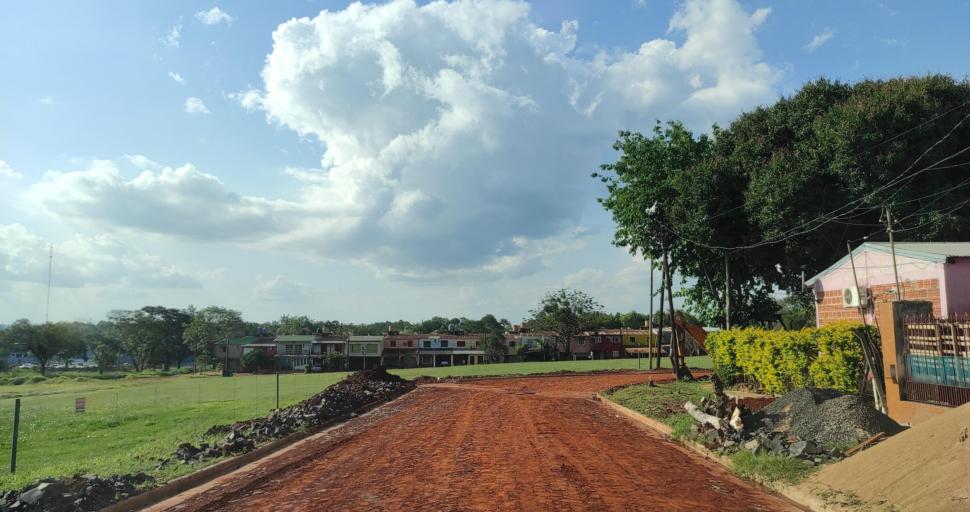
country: AR
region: Misiones
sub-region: Departamento de Capital
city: Posadas
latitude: -27.3607
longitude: -55.9251
